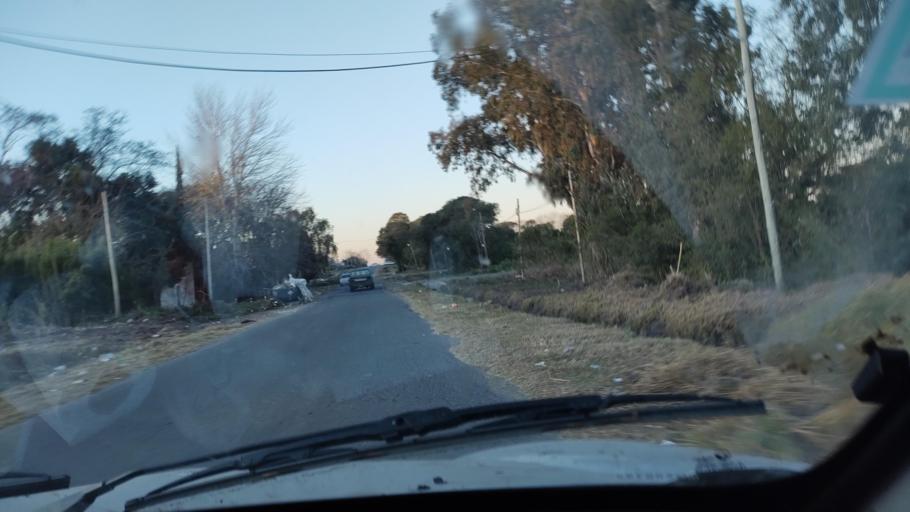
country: AR
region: Buenos Aires
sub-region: Partido de La Plata
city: La Plata
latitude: -34.9096
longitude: -58.0158
